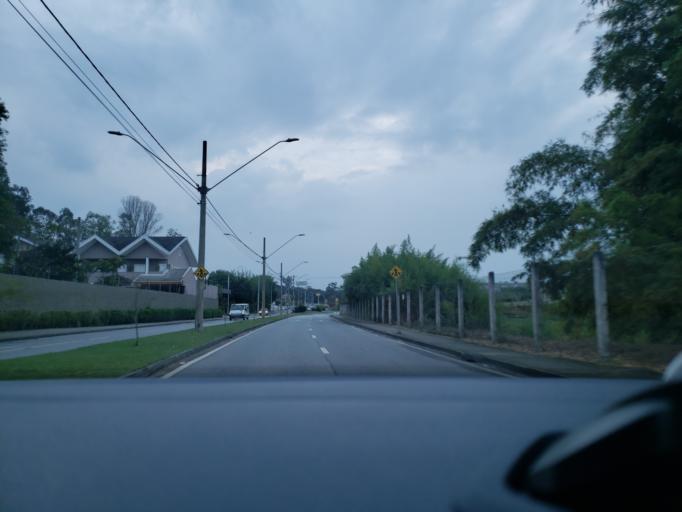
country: BR
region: Sao Paulo
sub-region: Sao Jose Dos Campos
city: Sao Jose dos Campos
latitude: -23.1968
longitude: -45.9438
